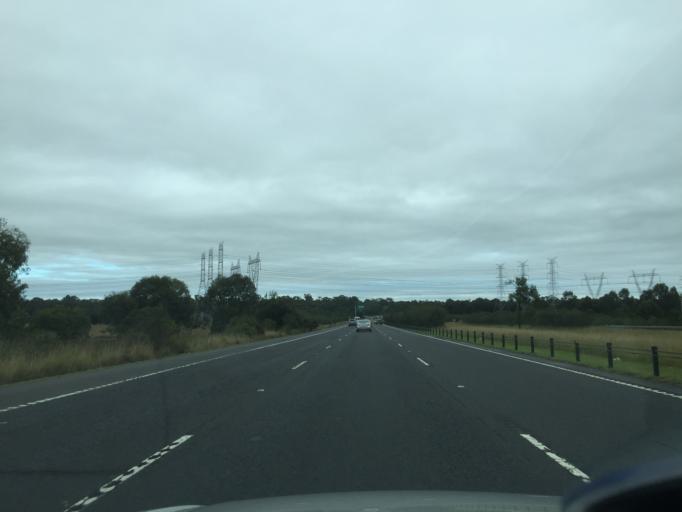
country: AU
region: New South Wales
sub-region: Blacktown
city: Mount Druitt
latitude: -33.7913
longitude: 150.8173
